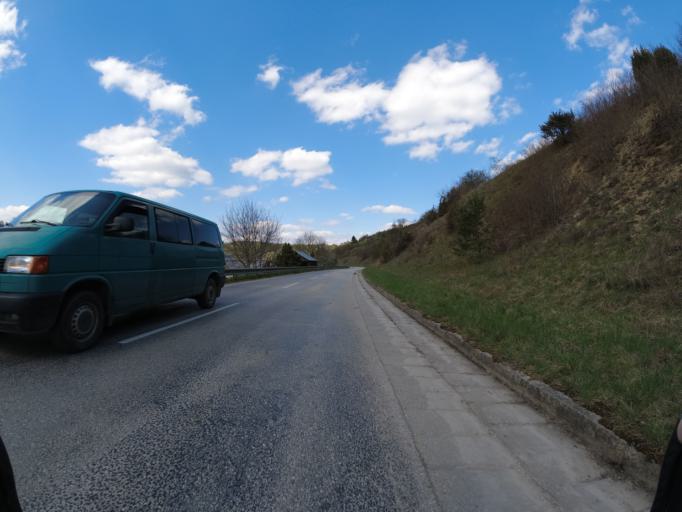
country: SK
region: Nitriansky
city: Stara Tura
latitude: 48.7451
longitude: 17.7220
